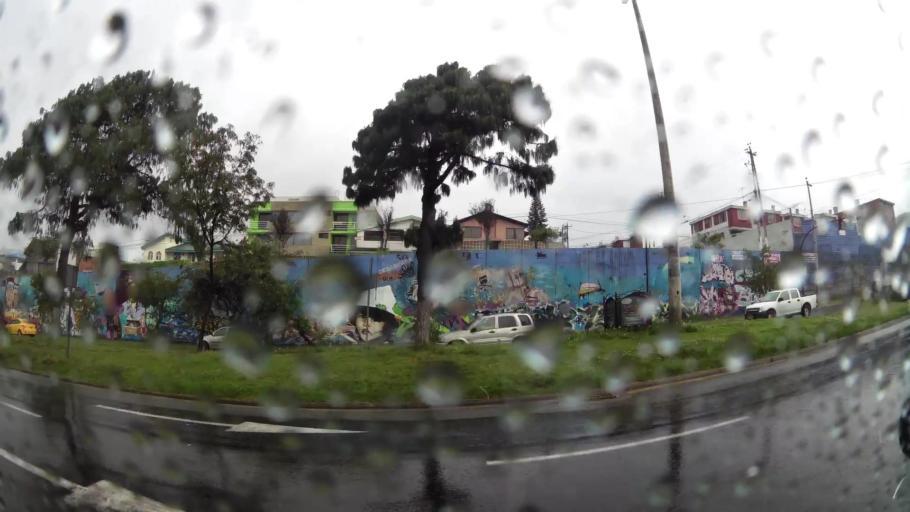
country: EC
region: Pichincha
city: Quito
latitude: -0.1055
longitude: -78.4995
